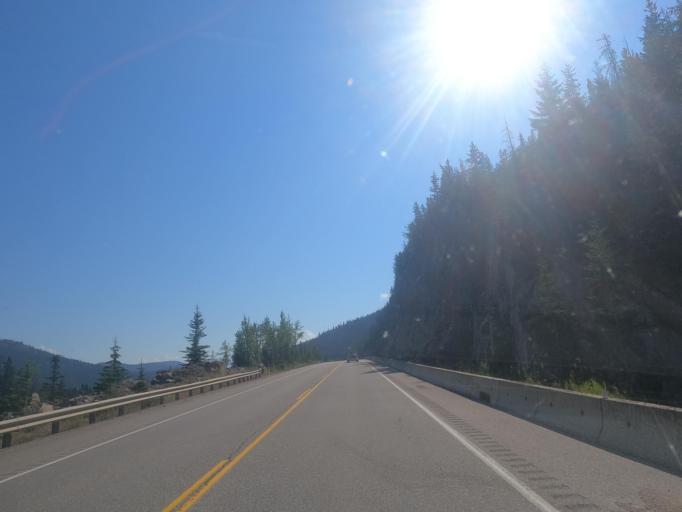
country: CA
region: Alberta
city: Jasper Park Lodge
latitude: 52.8746
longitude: -118.3093
